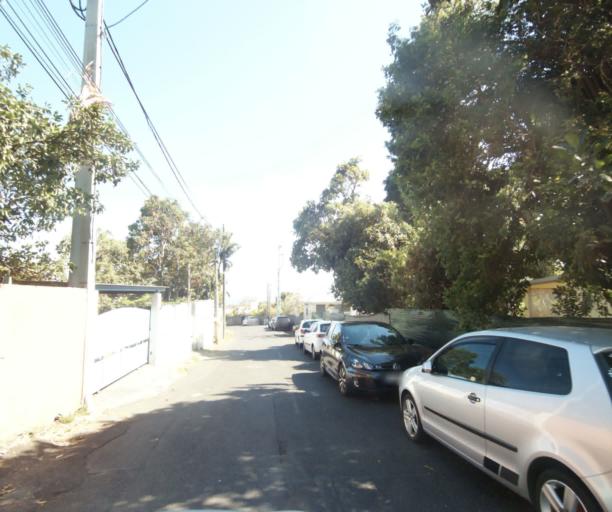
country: RE
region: Reunion
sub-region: Reunion
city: La Possession
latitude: -20.9814
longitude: 55.3326
